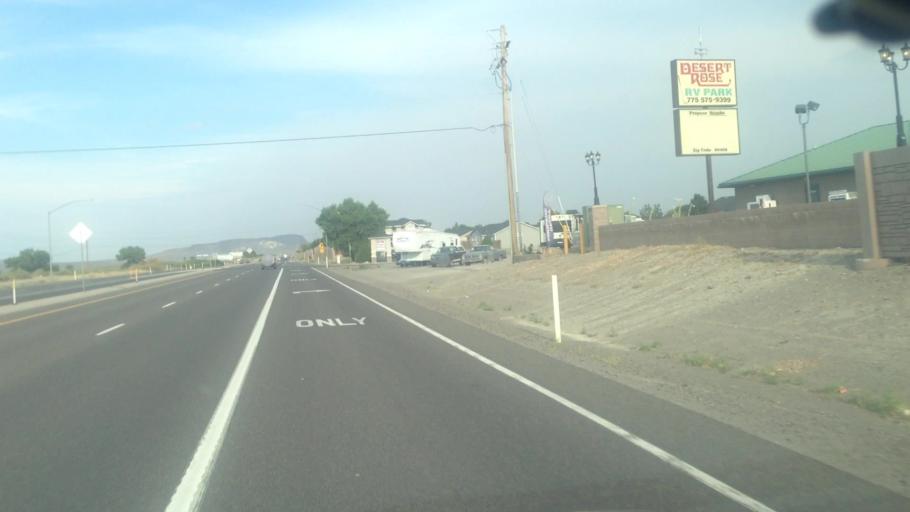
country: US
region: Nevada
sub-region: Lyon County
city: Fernley
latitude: 39.5928
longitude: -119.1567
